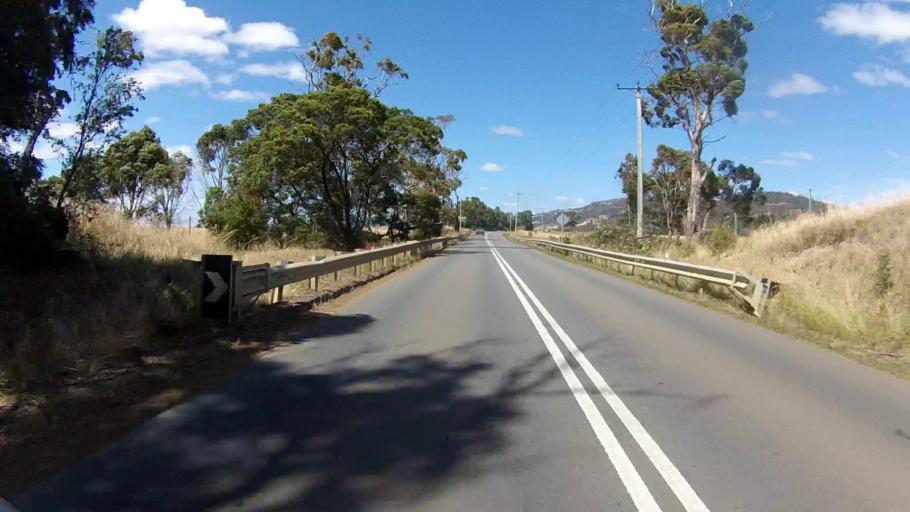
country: AU
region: Tasmania
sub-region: Clarence
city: Cambridge
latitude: -42.7680
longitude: 147.4161
